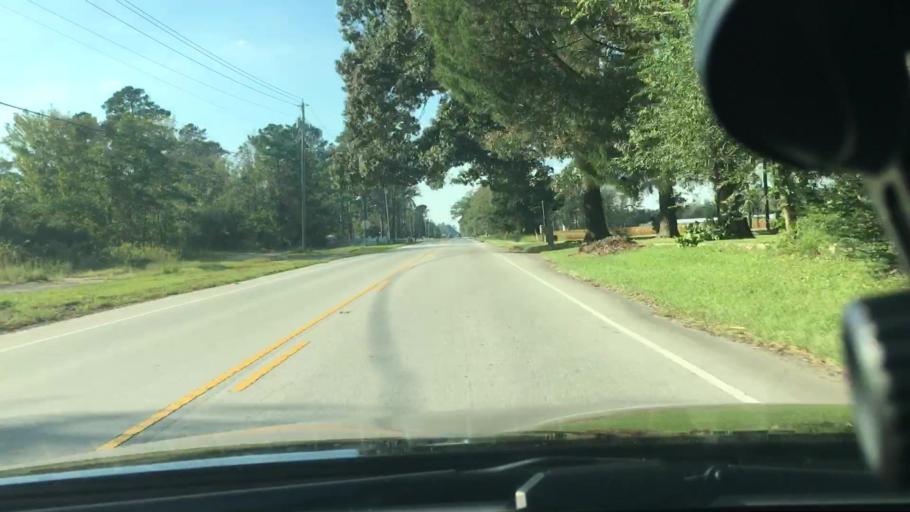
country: US
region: North Carolina
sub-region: Craven County
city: Vanceboro
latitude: 35.2393
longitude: -77.0775
